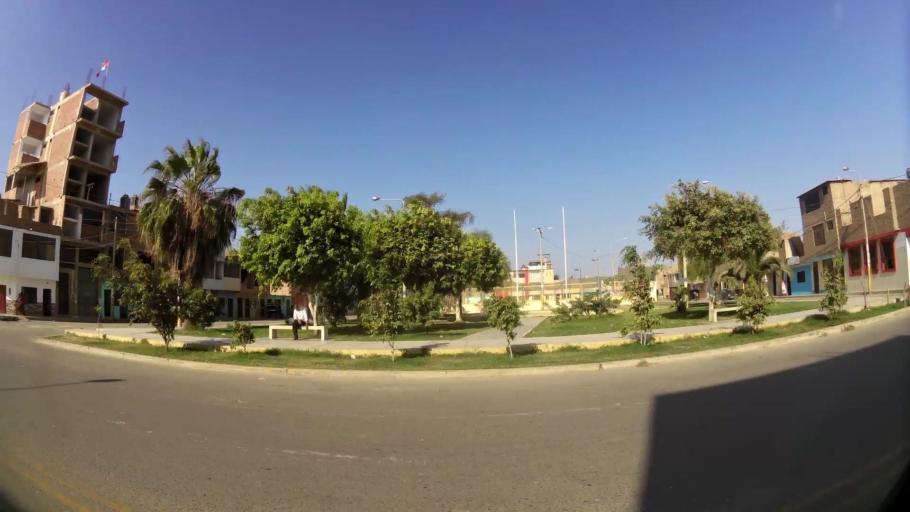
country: PE
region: Lambayeque
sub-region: Provincia de Chiclayo
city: Chiclayo
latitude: -6.7663
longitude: -79.8456
